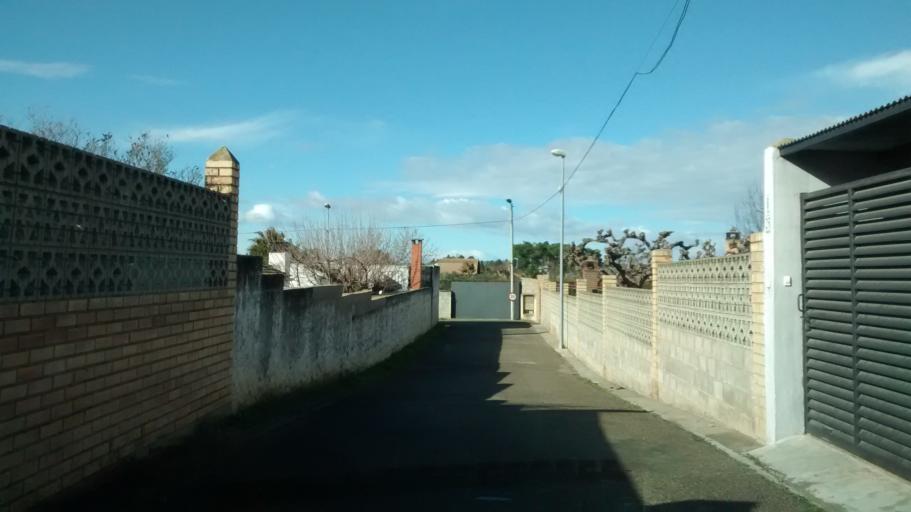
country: ES
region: Aragon
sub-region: Provincia de Zaragoza
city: Villanueva de Gallego
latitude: 41.7348
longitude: -0.7978
